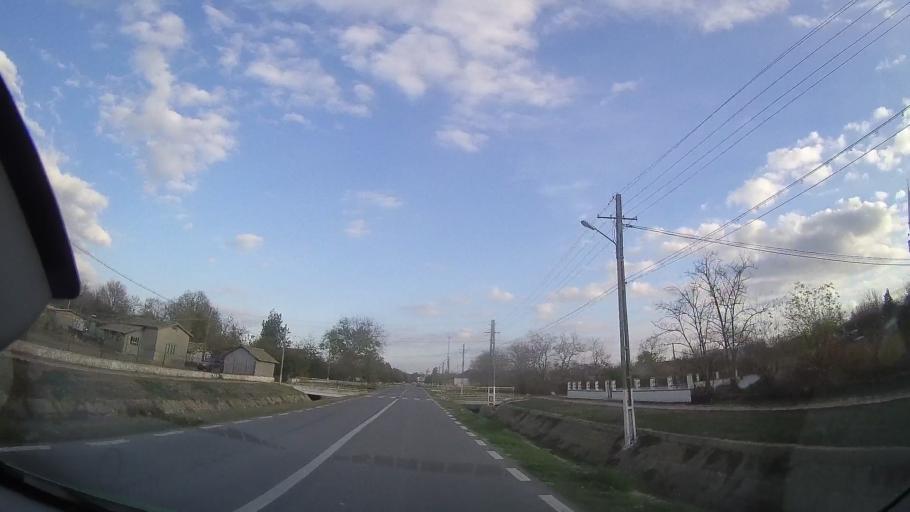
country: RO
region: Constanta
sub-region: Comuna Independenta
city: Independenta
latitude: 43.9535
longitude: 28.0782
